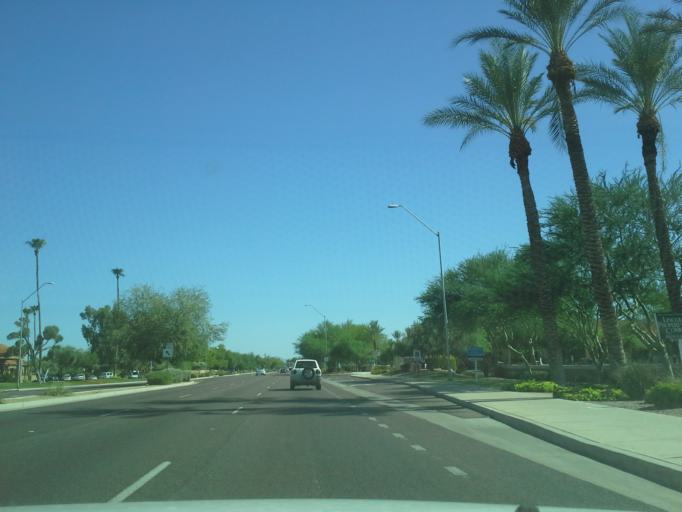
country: US
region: Arizona
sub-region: Maricopa County
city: Paradise Valley
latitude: 33.5403
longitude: -111.9256
